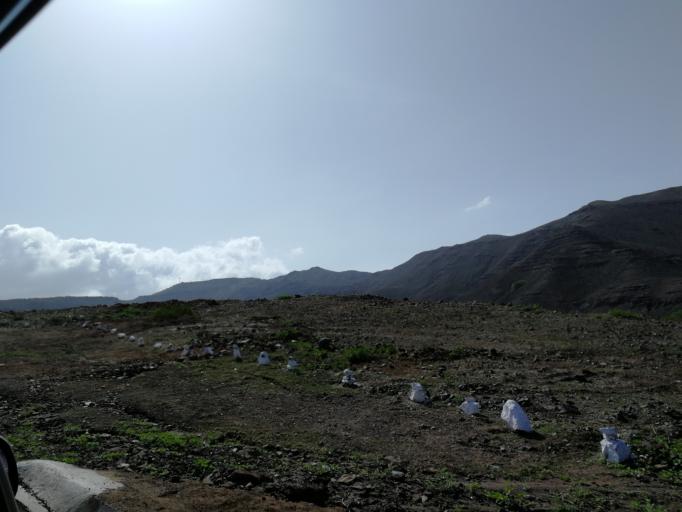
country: CV
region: Sao Vicente
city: Mindelo
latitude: 16.8880
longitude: -24.9401
